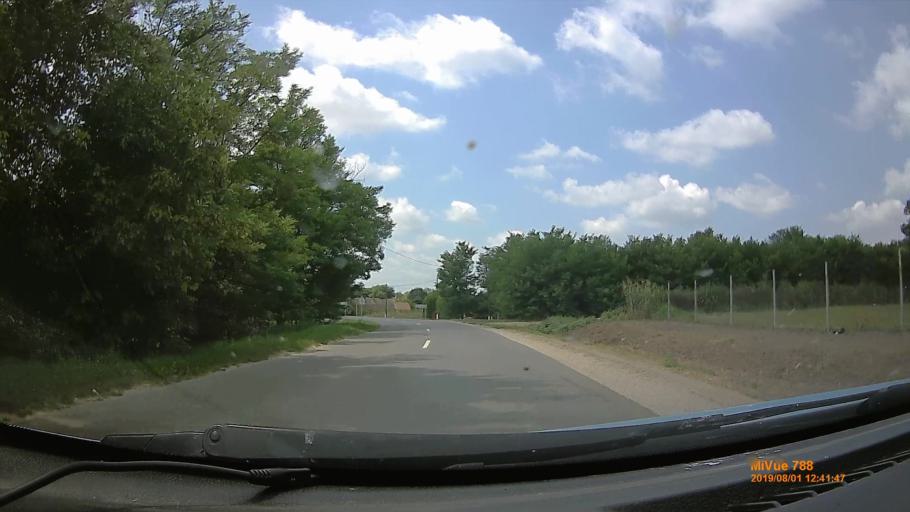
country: HU
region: Baranya
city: Harkany
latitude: 45.8372
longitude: 18.1706
